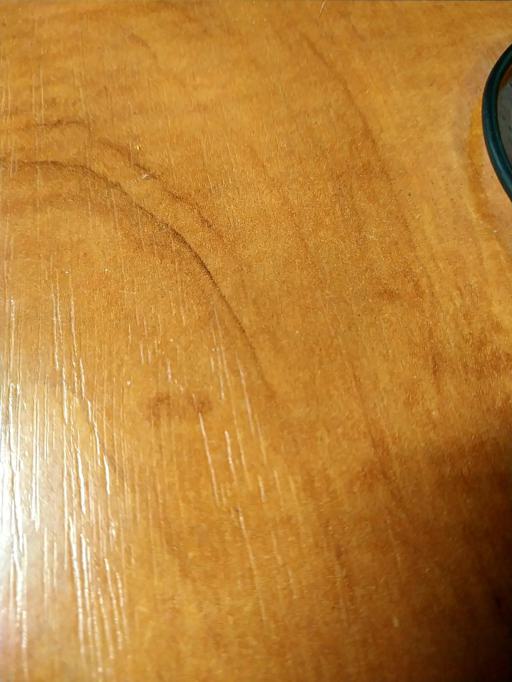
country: RU
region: Smolensk
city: Yartsevo
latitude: 55.4264
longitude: 32.8277
